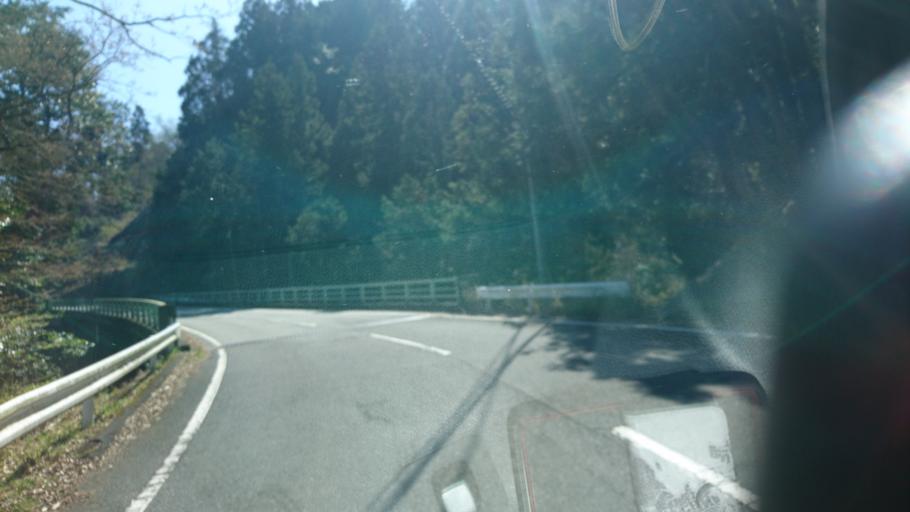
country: JP
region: Shizuoka
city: Fujinomiya
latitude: 35.3515
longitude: 138.4371
